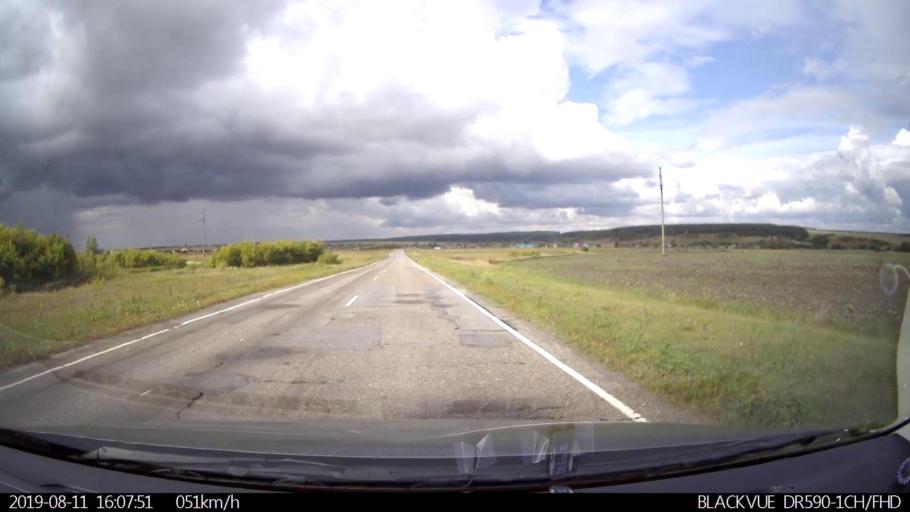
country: RU
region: Ulyanovsk
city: Ignatovka
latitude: 53.9802
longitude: 47.6469
